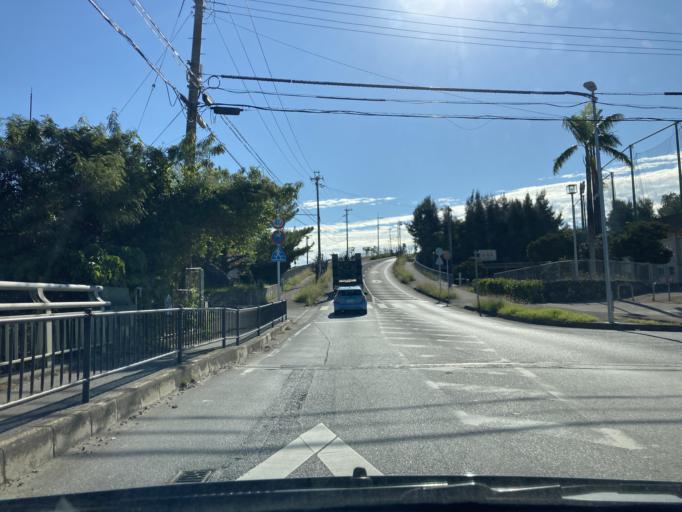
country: JP
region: Okinawa
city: Okinawa
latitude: 26.3703
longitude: 127.7702
